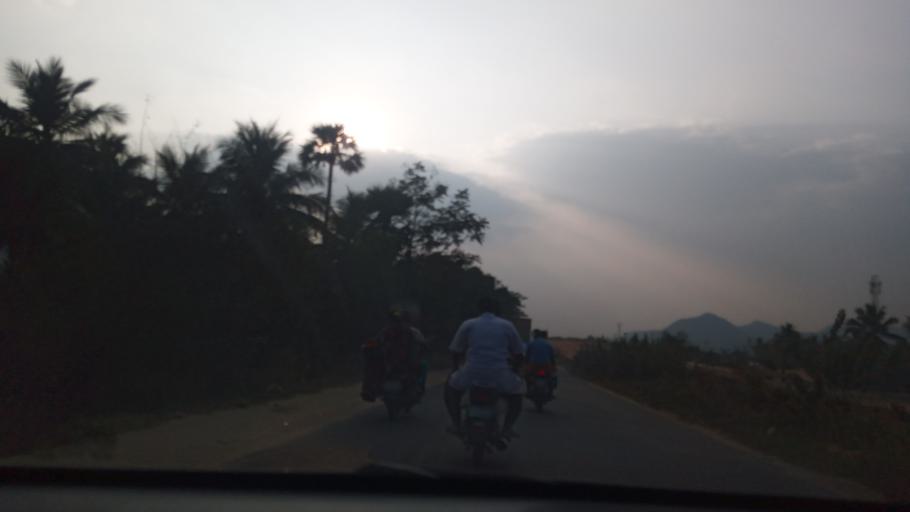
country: IN
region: Tamil Nadu
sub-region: Salem
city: Idappadi
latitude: 11.4939
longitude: 77.8701
